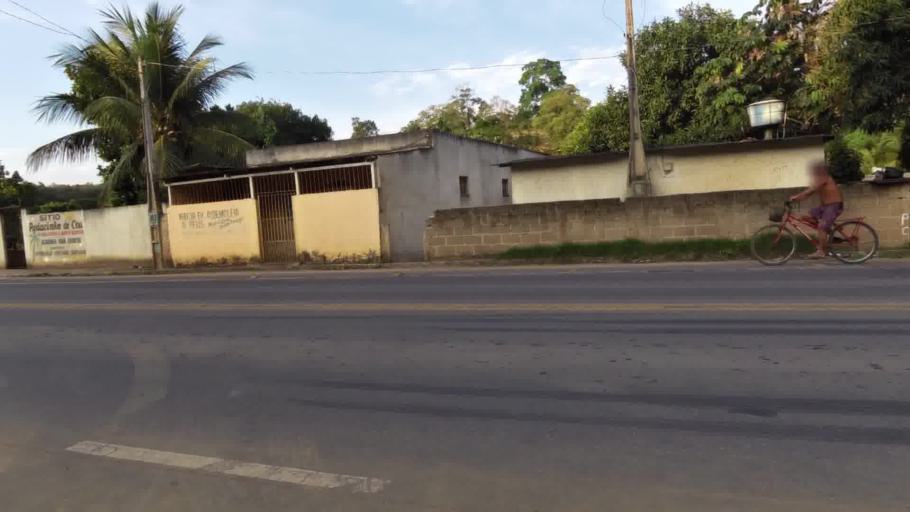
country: BR
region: Espirito Santo
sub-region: Piuma
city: Piuma
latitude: -20.8252
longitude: -40.7319
